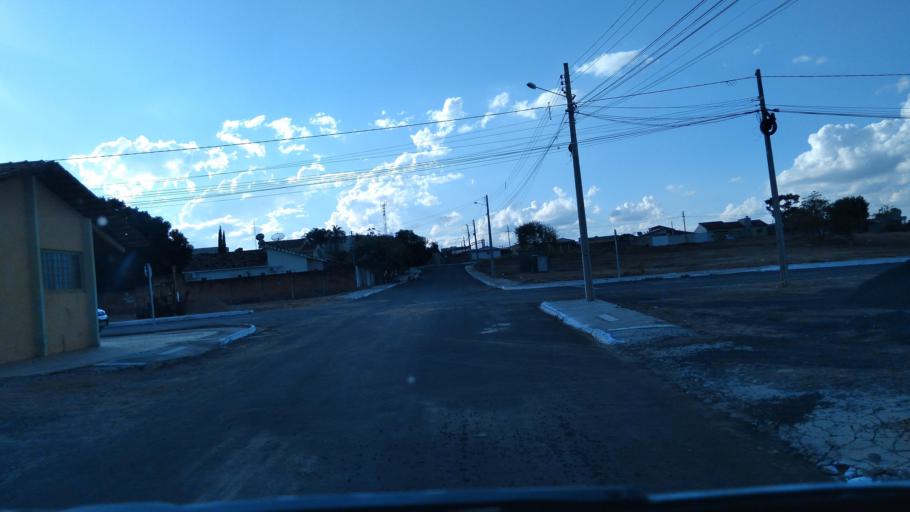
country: BR
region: Goias
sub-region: Mineiros
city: Mineiros
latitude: -17.5584
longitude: -52.5489
